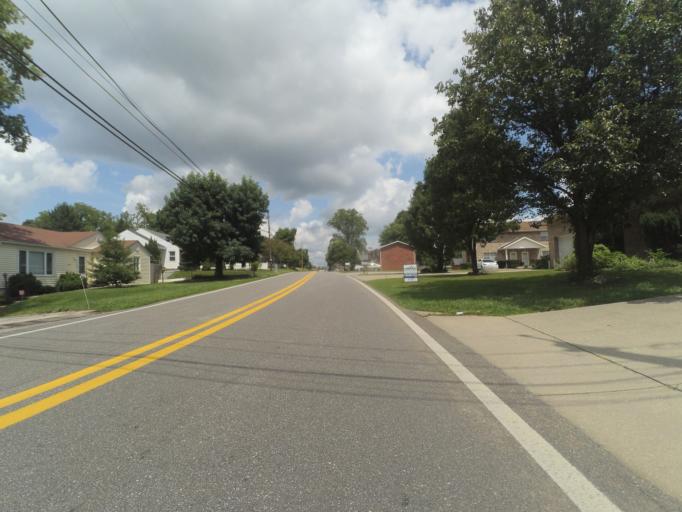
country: US
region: West Virginia
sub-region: Cabell County
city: Pea Ridge
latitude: 38.4092
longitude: -82.3425
